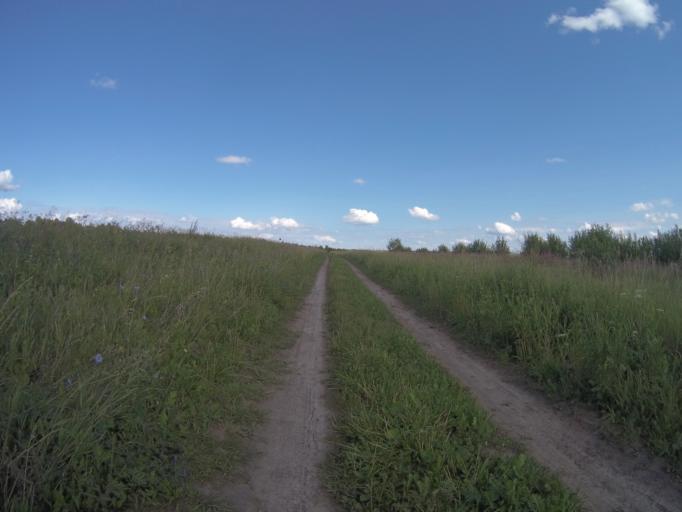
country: RU
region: Vladimir
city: Vladimir
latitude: 56.2901
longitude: 40.3563
